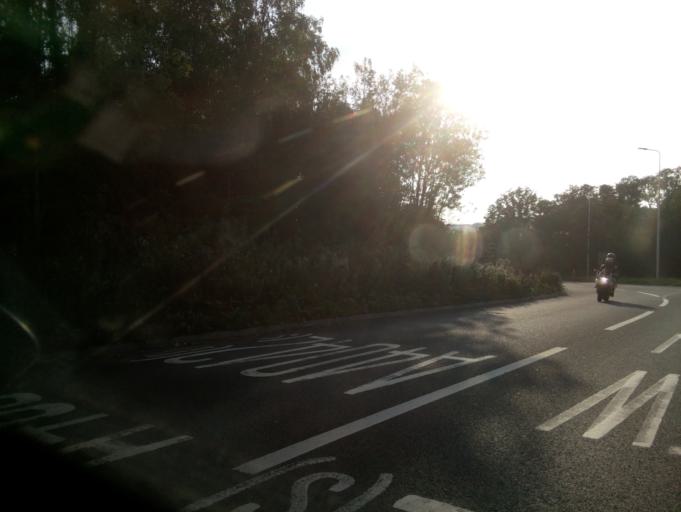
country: GB
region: Wales
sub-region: Torfaen County Borough
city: New Inn
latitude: 51.6817
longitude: -3.0145
